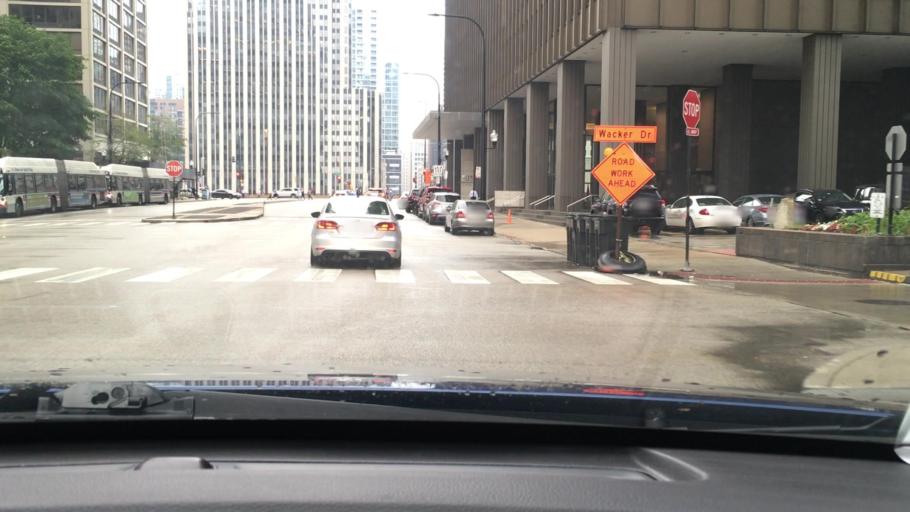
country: US
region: Illinois
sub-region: Cook County
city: Chicago
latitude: 41.8866
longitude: -87.6206
